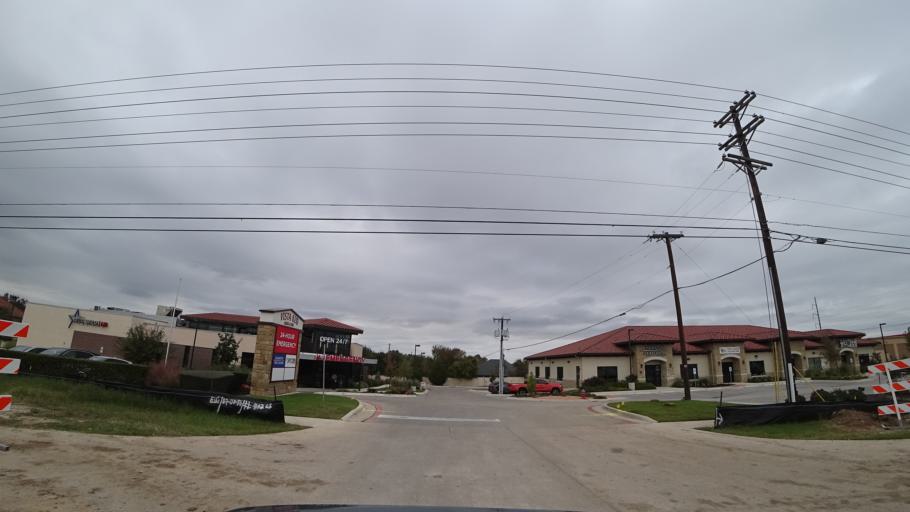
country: US
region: Texas
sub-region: Williamson County
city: Round Rock
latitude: 30.5127
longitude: -97.7030
